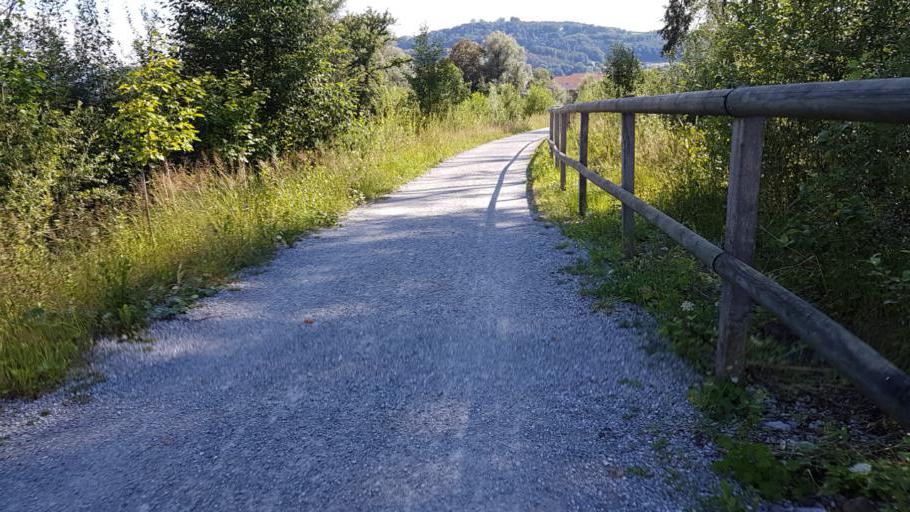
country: CH
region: Bern
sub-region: Bern-Mittelland District
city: Muri
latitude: 46.9237
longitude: 7.4821
